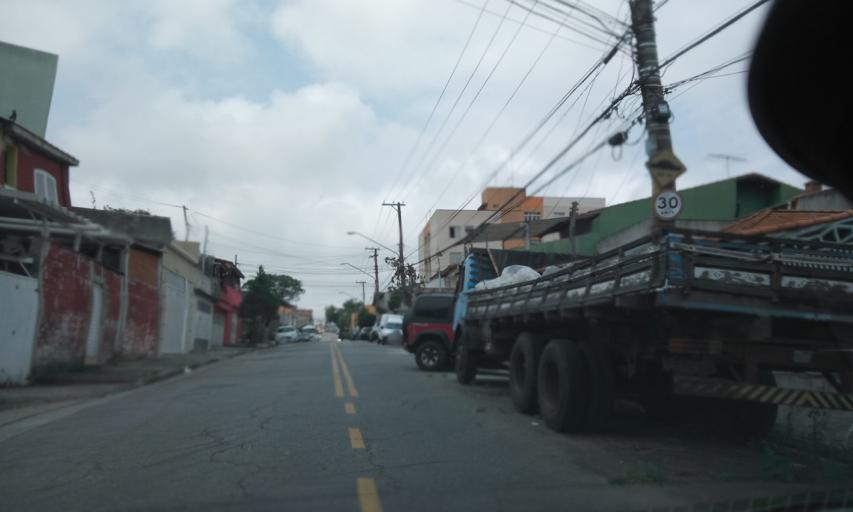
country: BR
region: Sao Paulo
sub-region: Sao Bernardo Do Campo
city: Sao Bernardo do Campo
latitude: -23.7018
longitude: -46.5757
